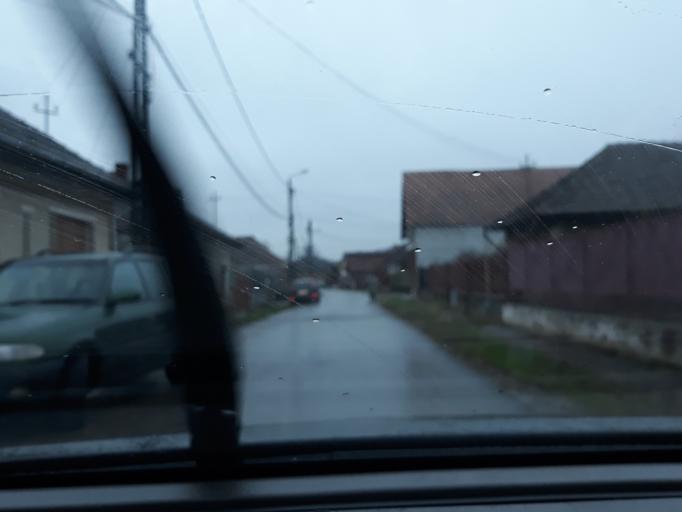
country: RO
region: Bihor
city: Margita
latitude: 47.3490
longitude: 22.3494
